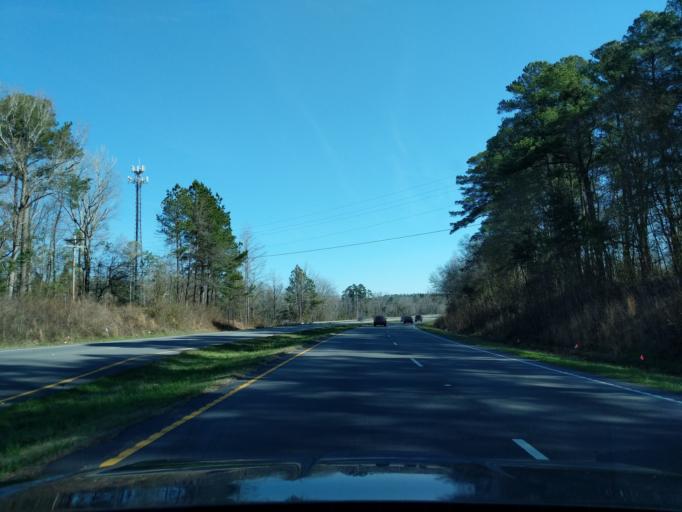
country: US
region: South Carolina
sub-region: Aiken County
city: Warrenville
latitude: 33.5510
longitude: -81.8190
